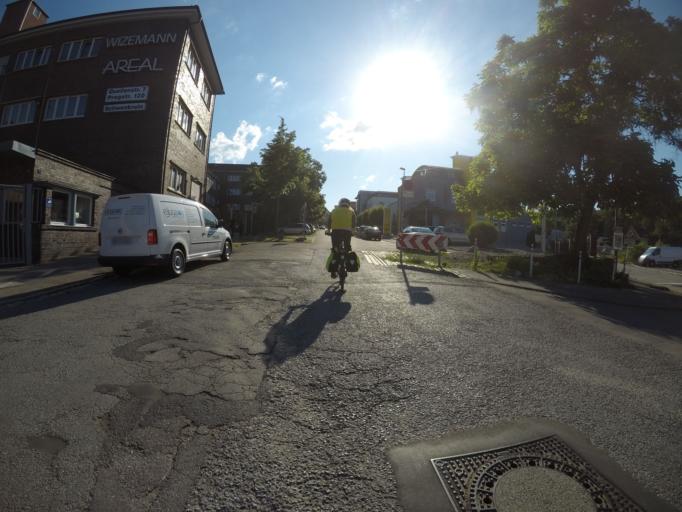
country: DE
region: Baden-Wuerttemberg
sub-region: Regierungsbezirk Stuttgart
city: Stuttgart-Ost
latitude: 48.8083
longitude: 9.2013
